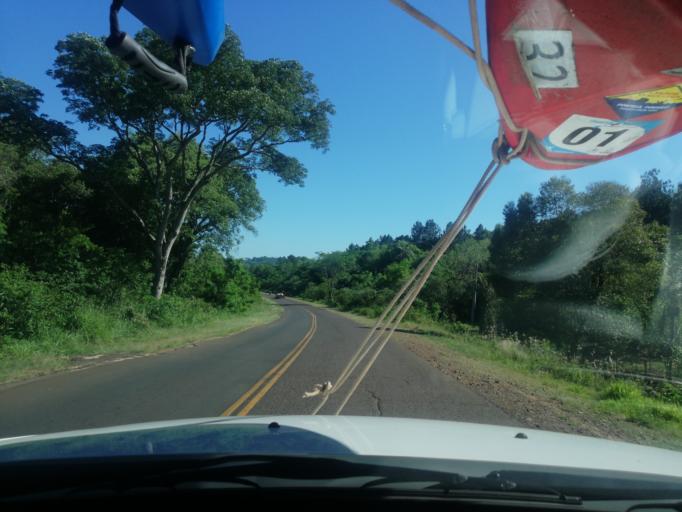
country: AR
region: Misiones
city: Santa Ana
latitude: -27.3513
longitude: -55.5832
